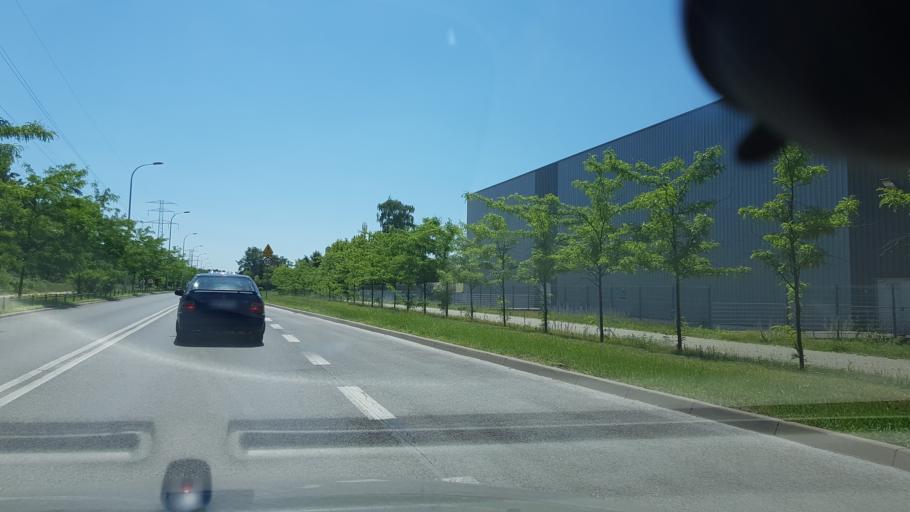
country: PL
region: Masovian Voivodeship
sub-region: Warszawa
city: Rembertow
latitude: 52.2413
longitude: 21.1399
